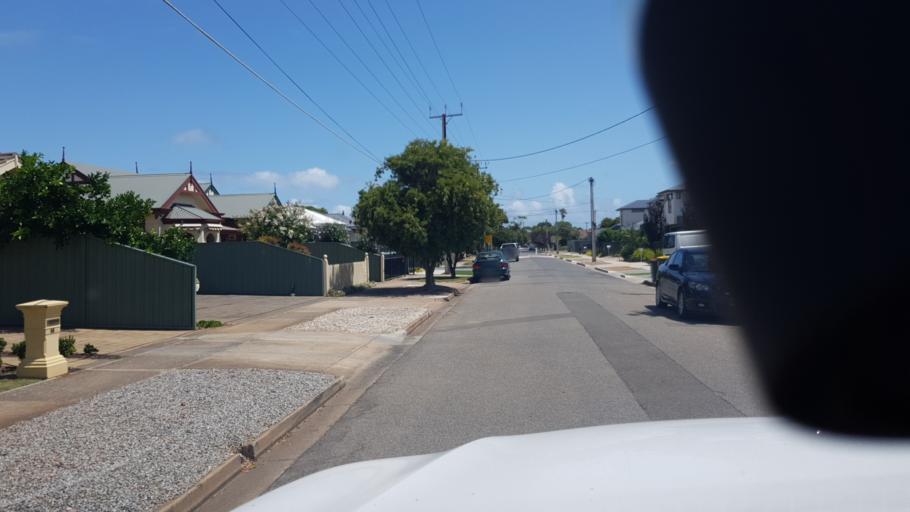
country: AU
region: South Australia
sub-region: Holdfast Bay
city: North Brighton
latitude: -34.9921
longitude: 138.5306
